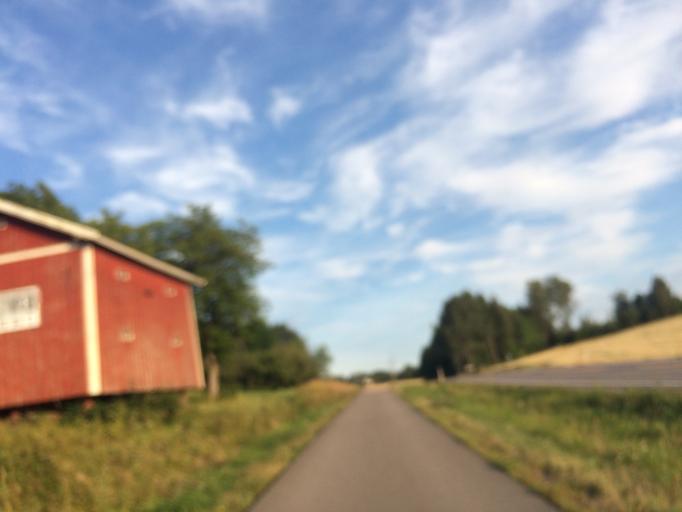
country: NO
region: Ostfold
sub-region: Hobol
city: Elvestad
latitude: 59.6684
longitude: 10.9006
